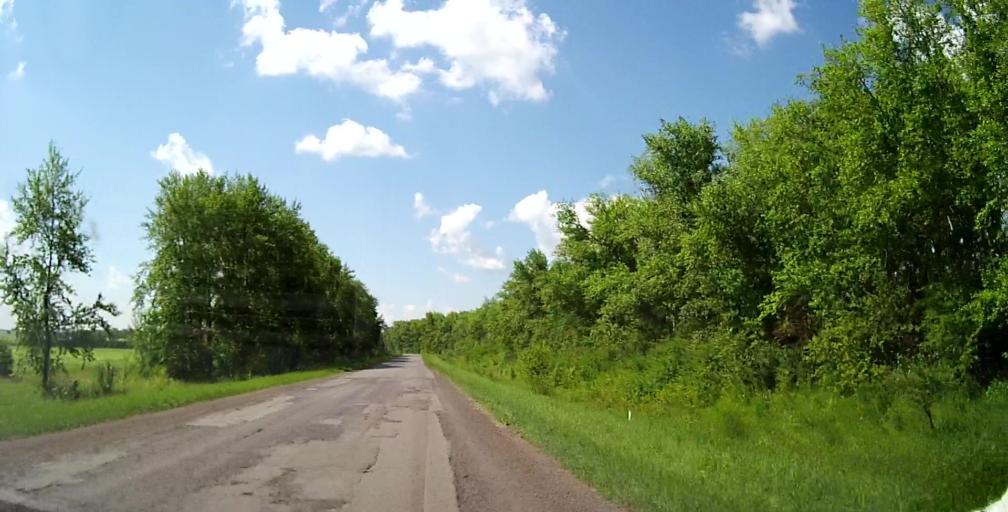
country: RU
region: Lipetsk
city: Chaplygin
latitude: 53.3093
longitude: 39.9549
